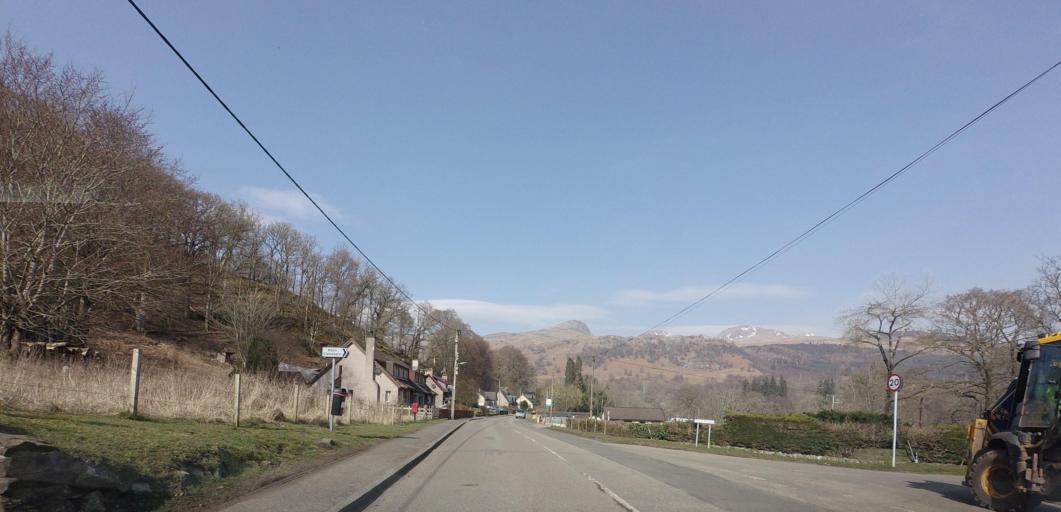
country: GB
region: Scotland
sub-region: Stirling
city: Callander
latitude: 56.4729
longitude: -4.3213
